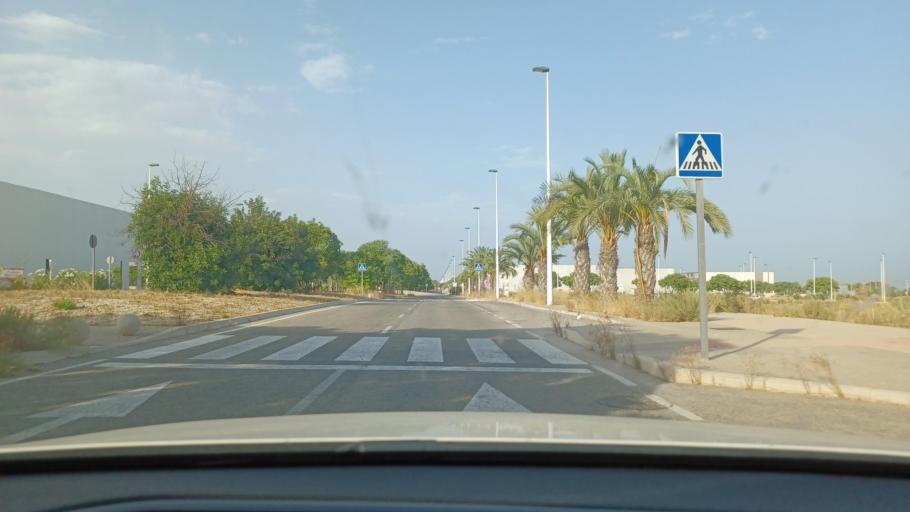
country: ES
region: Valencia
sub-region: Provincia de Alicante
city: Elche
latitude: 38.2869
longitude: -0.6228
